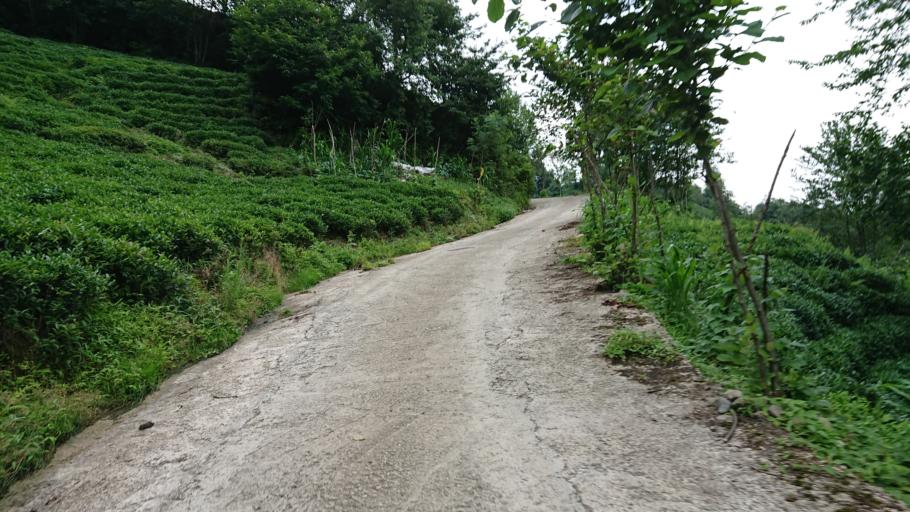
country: TR
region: Rize
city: Rize
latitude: 40.9671
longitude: 40.5160
